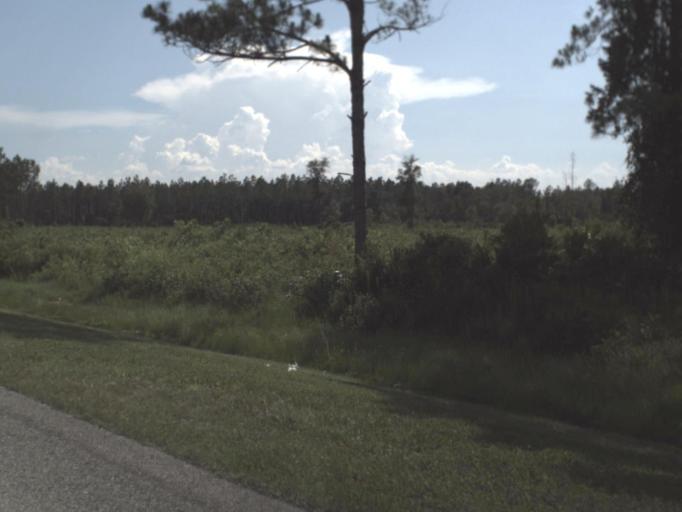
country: US
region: Florida
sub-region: Marion County
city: Citra
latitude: 29.4953
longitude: -82.0998
